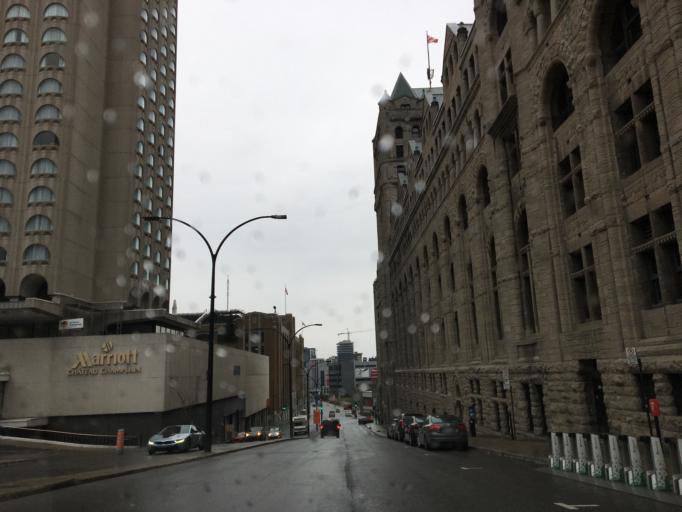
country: CA
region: Quebec
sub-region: Montreal
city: Montreal
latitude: 45.4976
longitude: -73.5685
